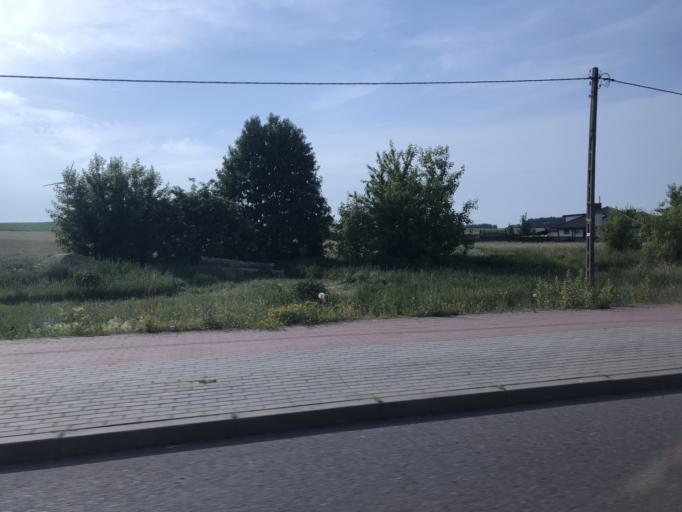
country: PL
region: Podlasie
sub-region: Lomza
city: Lomza
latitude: 53.1575
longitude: 22.0306
